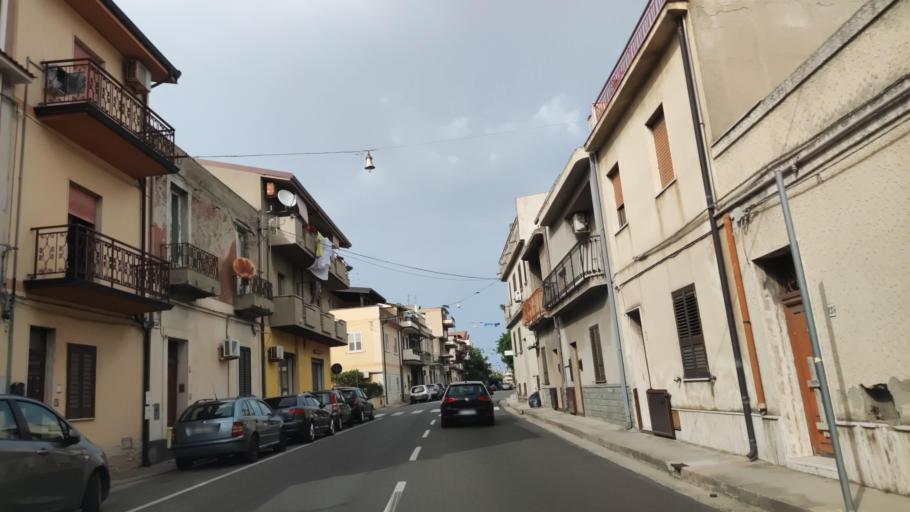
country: IT
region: Calabria
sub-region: Provincia di Reggio Calabria
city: Siderno
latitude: 38.2617
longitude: 16.2892
